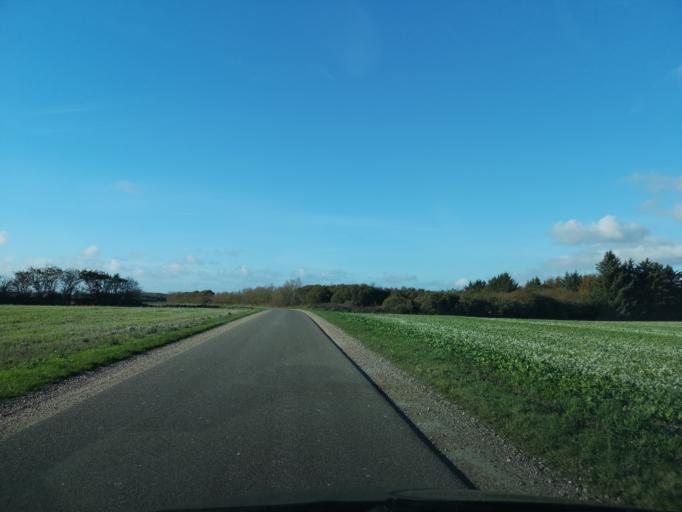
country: DK
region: Central Jutland
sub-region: Ringkobing-Skjern Kommune
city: Tarm
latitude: 55.8107
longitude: 8.4389
